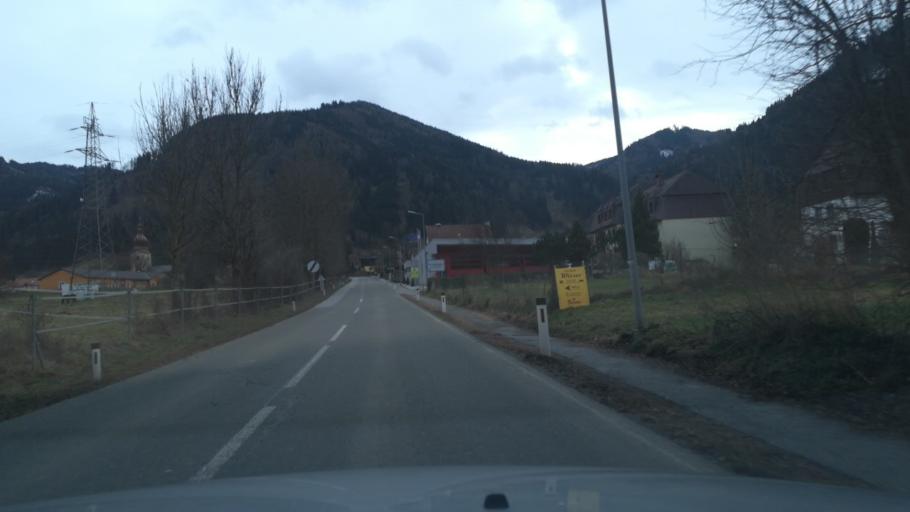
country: AT
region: Styria
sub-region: Politischer Bezirk Murtal
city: Sankt Georgen ob Judenburg
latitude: 47.2106
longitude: 14.4983
